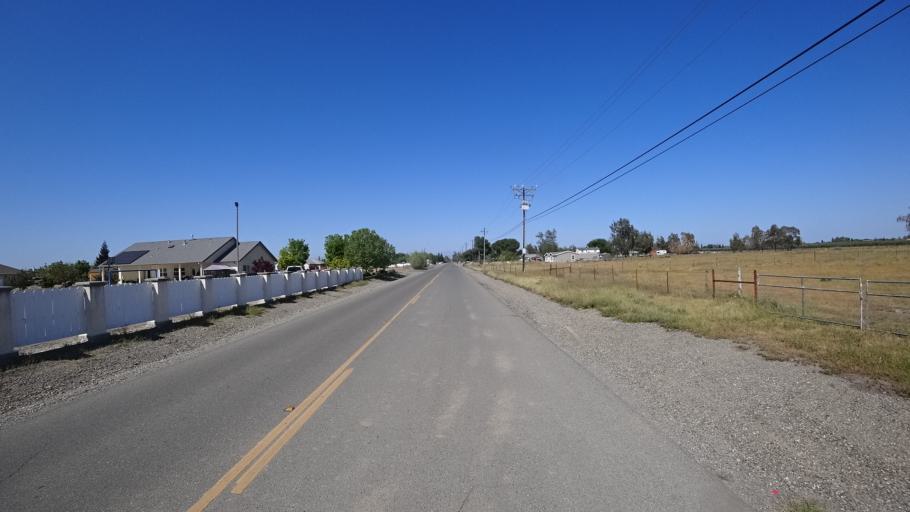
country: US
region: California
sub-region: Glenn County
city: Orland
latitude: 39.7254
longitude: -122.1694
